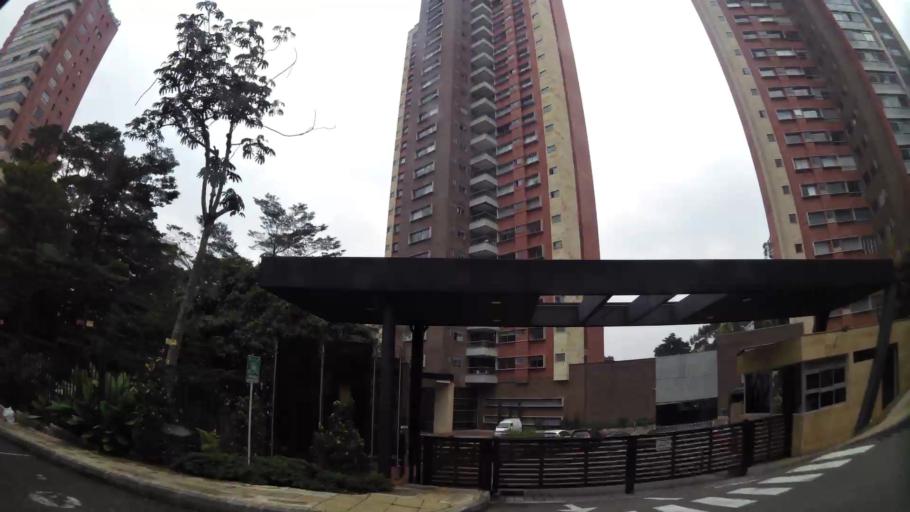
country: CO
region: Antioquia
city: Envigado
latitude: 6.2064
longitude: -75.5577
